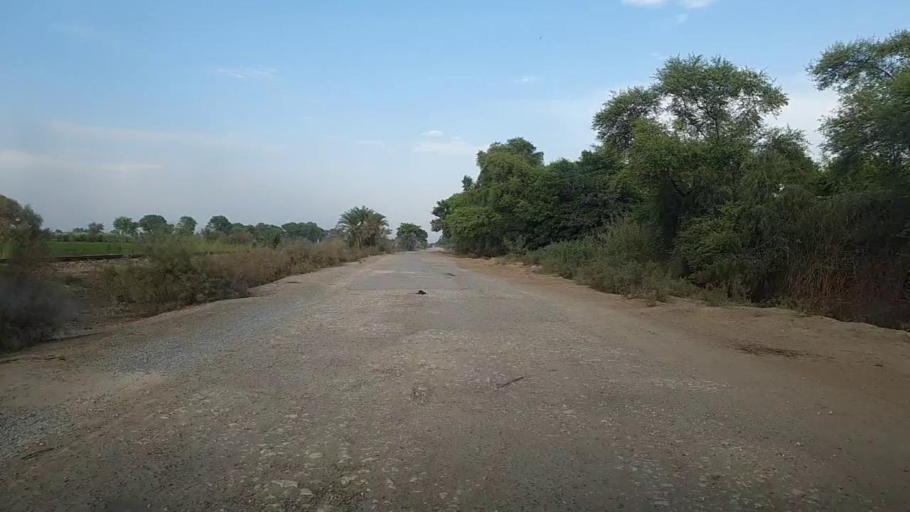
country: PK
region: Sindh
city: Thul
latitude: 28.2916
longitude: 68.8743
